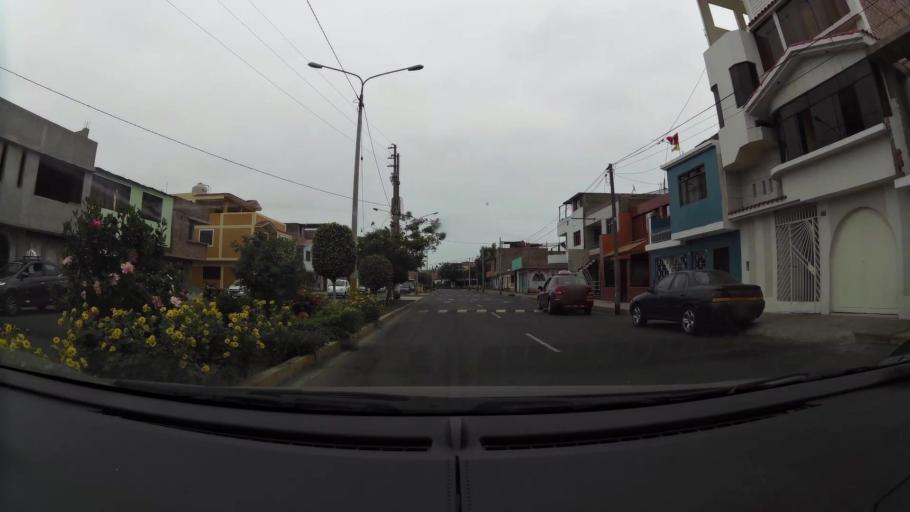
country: PE
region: Ancash
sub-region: Provincia de Santa
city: Chimbote
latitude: -9.0676
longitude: -78.5972
